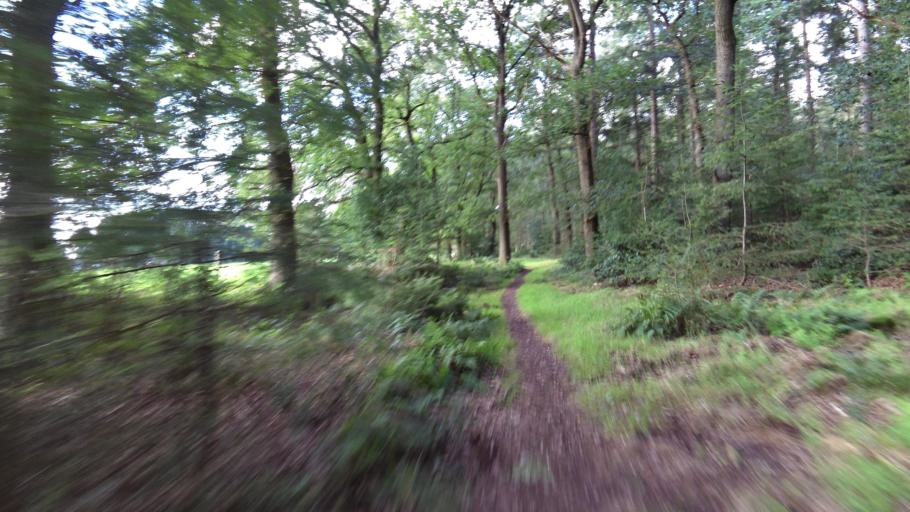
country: NL
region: Gelderland
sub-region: Gemeente Apeldoorn
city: Uddel
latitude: 52.2598
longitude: 5.7942
